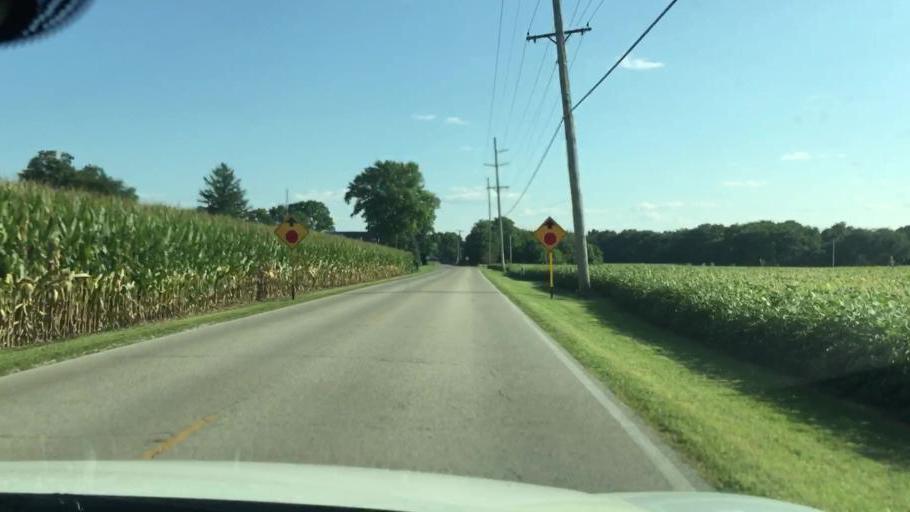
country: US
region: Ohio
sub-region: Clark County
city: Northridge
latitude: 39.9409
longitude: -83.7104
